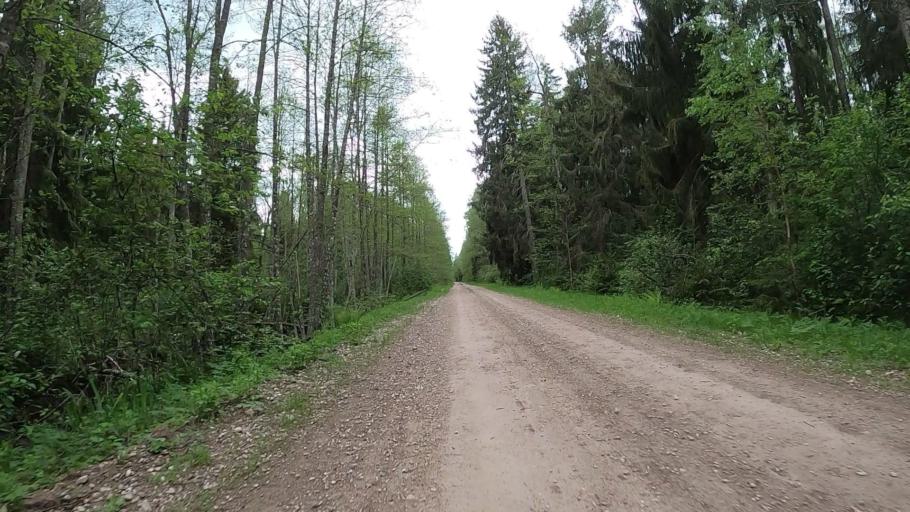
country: LV
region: Ozolnieku
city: Ozolnieki
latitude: 56.8079
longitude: 23.7866
